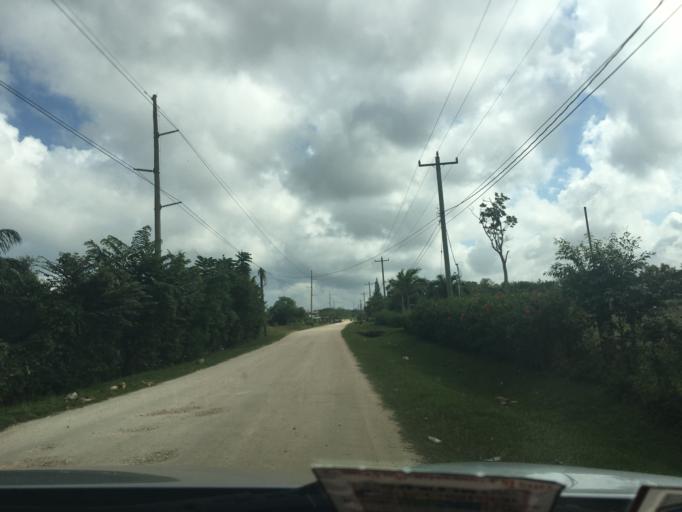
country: BZ
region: Cayo
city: Belmopan
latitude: 17.2510
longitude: -88.7923
